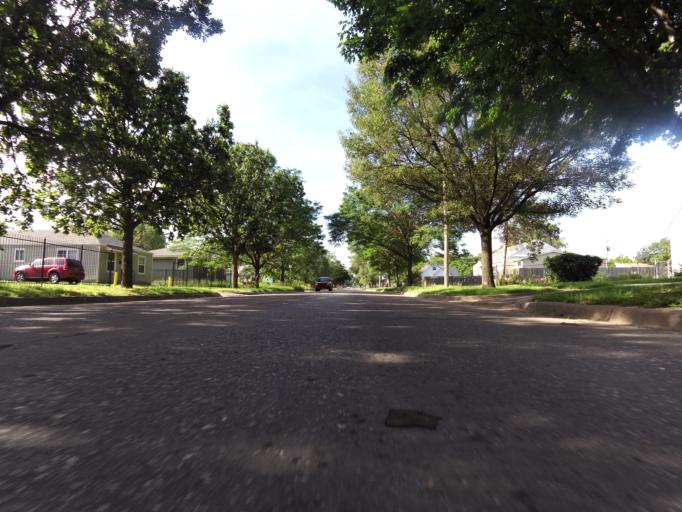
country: US
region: Kansas
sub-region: Sedgwick County
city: Wichita
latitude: 37.7070
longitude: -97.3082
